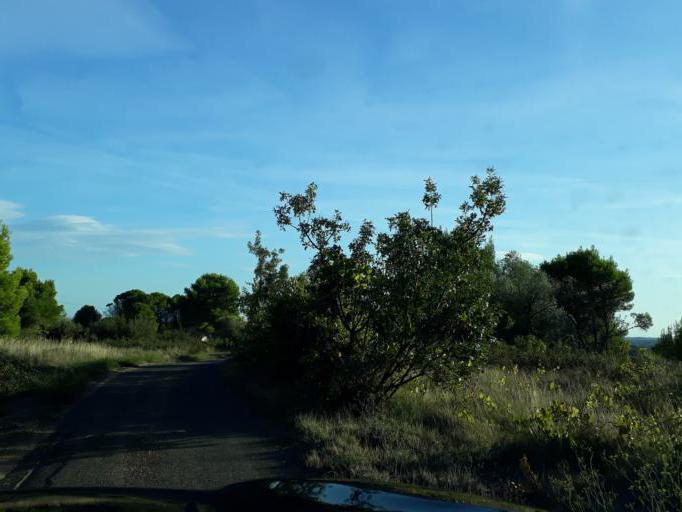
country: FR
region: Languedoc-Roussillon
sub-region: Departement de l'Herault
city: Florensac
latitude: 43.4205
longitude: 3.4735
